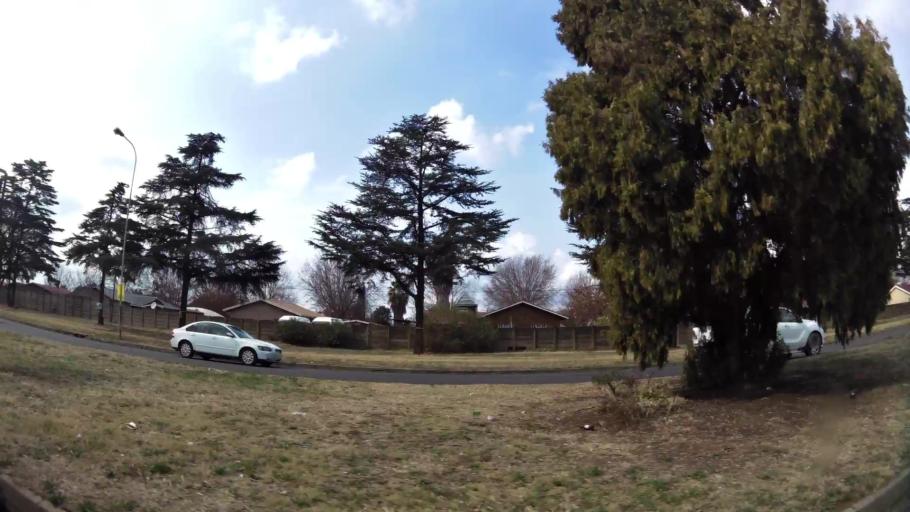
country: ZA
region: Gauteng
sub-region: Sedibeng District Municipality
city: Vanderbijlpark
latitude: -26.7105
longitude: 27.8360
